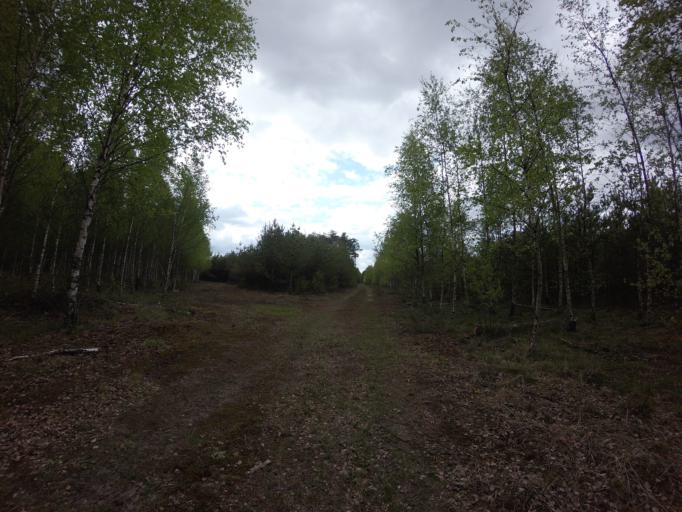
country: PL
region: West Pomeranian Voivodeship
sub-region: Powiat drawski
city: Kalisz Pomorski
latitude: 53.1913
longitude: 15.9801
